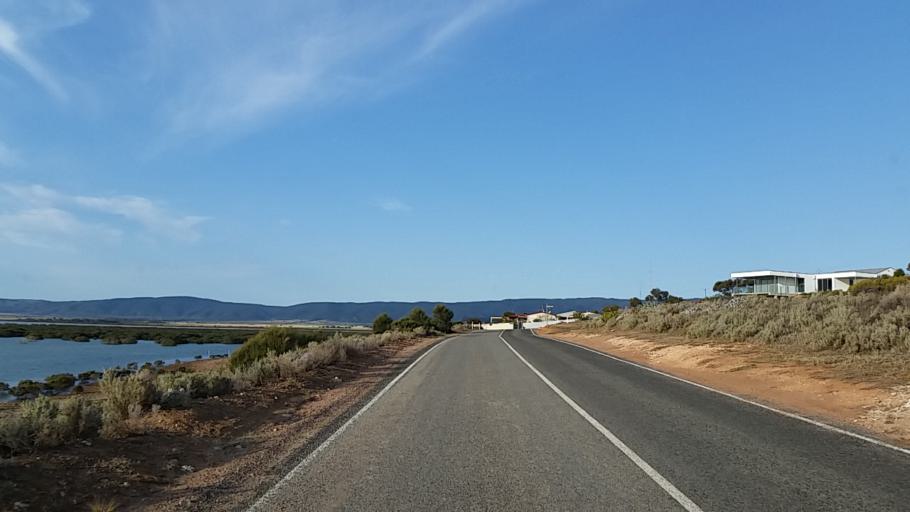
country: AU
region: South Australia
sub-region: Port Pirie City and Dists
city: Port Pirie
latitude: -33.1023
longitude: 138.0255
